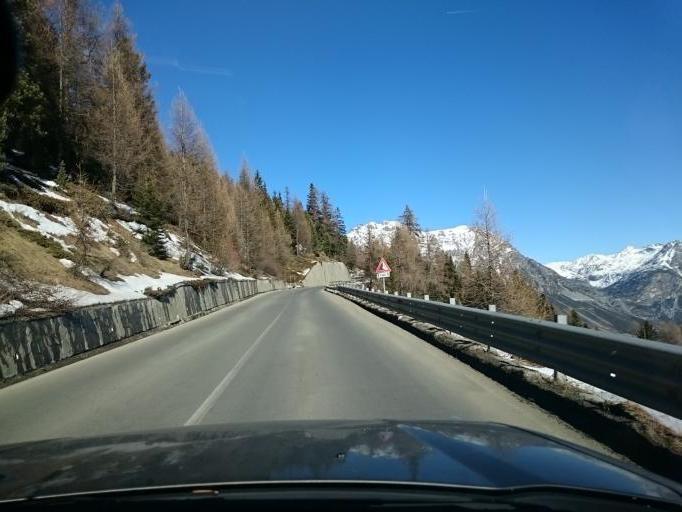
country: IT
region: Lombardy
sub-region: Provincia di Sondrio
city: Isolaccia
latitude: 46.4698
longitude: 10.2499
